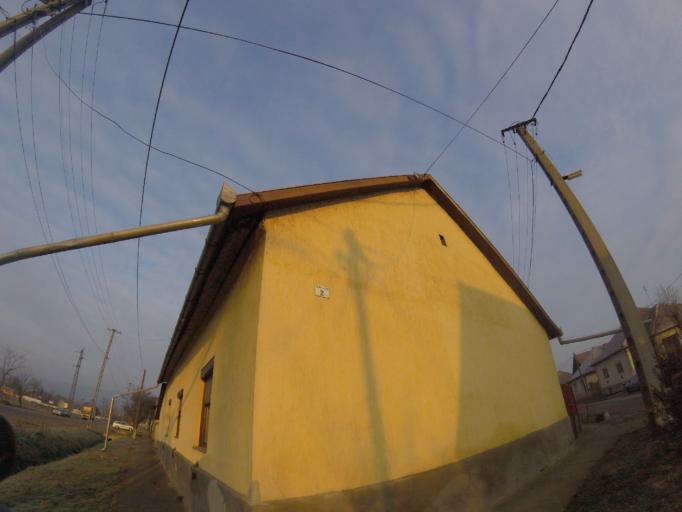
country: HU
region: Nograd
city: Paszto
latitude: 47.9237
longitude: 19.6857
